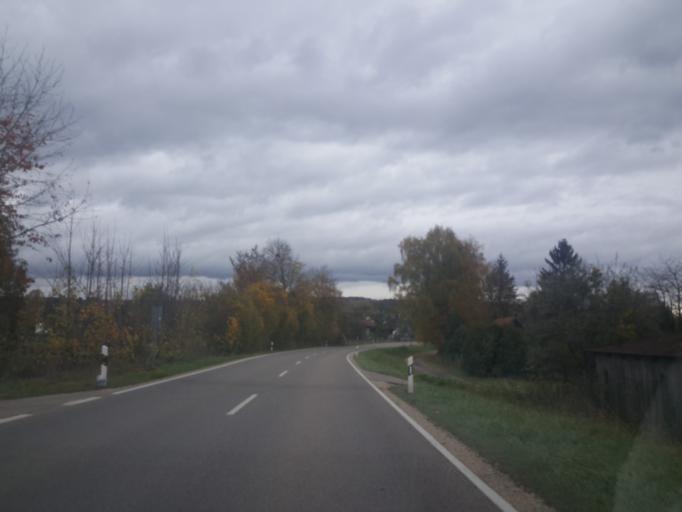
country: DE
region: Bavaria
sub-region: Upper Bavaria
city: Rennertshofen
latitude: 48.7547
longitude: 11.0402
